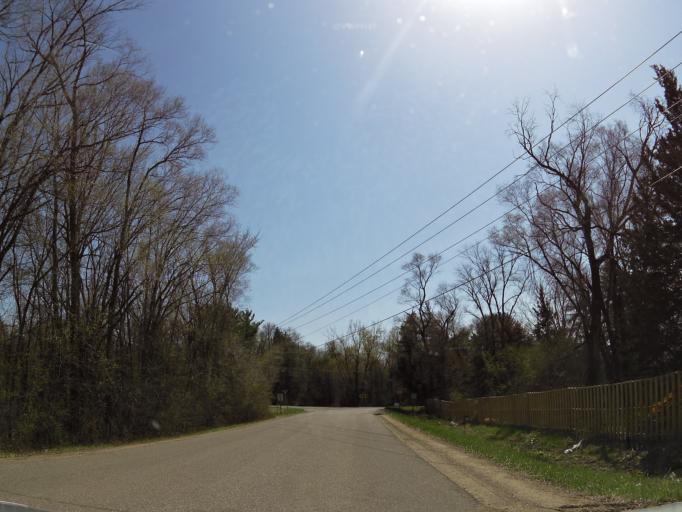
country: US
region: Wisconsin
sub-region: Saint Croix County
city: Hudson
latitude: 44.9803
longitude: -92.7058
